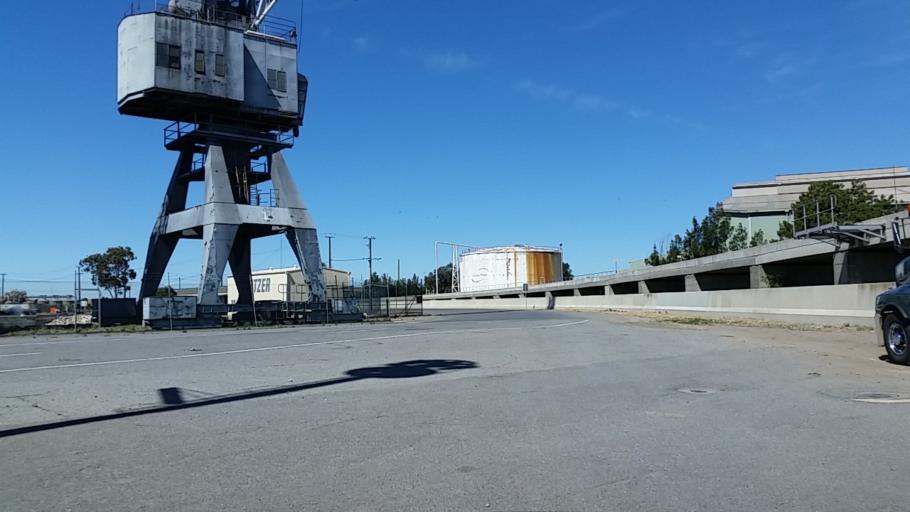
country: AU
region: South Australia
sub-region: Port Adelaide Enfield
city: Birkenhead
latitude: -34.8382
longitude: 138.5108
